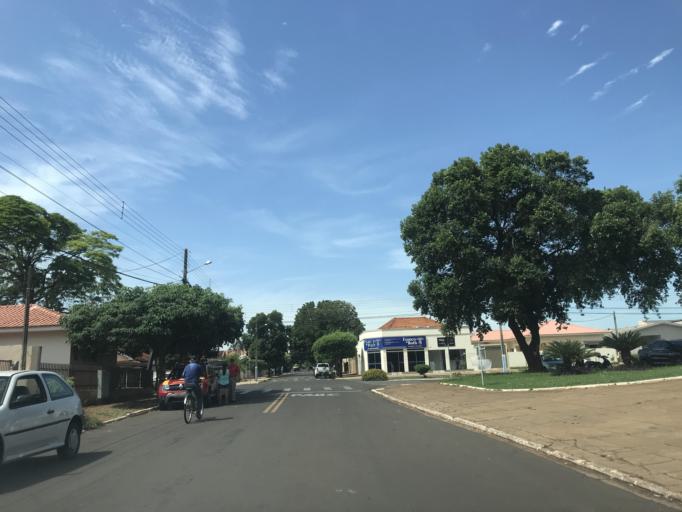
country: BR
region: Parana
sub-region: Terra Rica
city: Terra Rica
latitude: -22.7259
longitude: -52.6223
